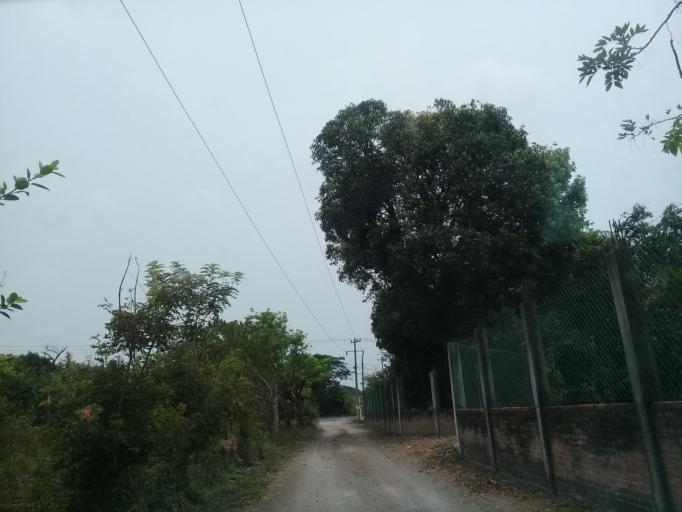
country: MX
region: Veracruz
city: El Tejar
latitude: 19.0451
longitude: -96.1943
